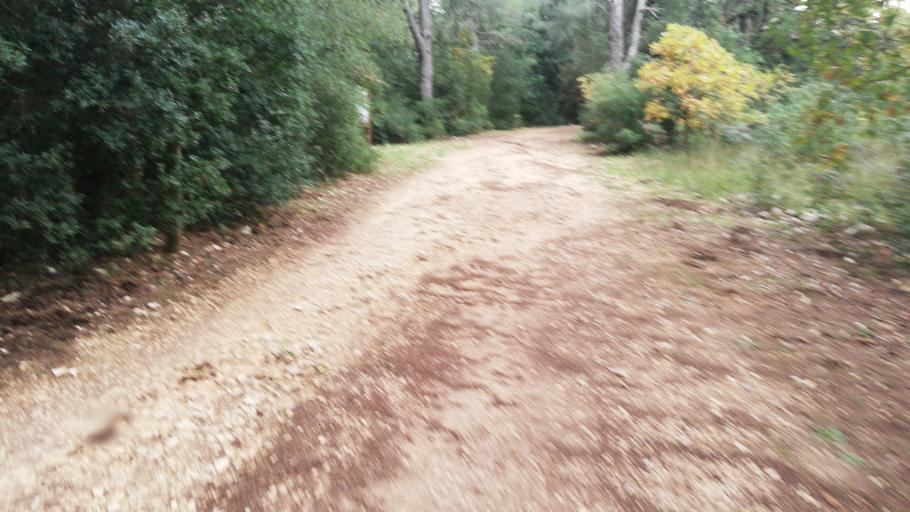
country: IT
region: Apulia
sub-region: Provincia di Bari
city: Cassano delle Murge
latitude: 40.8796
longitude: 16.7122
